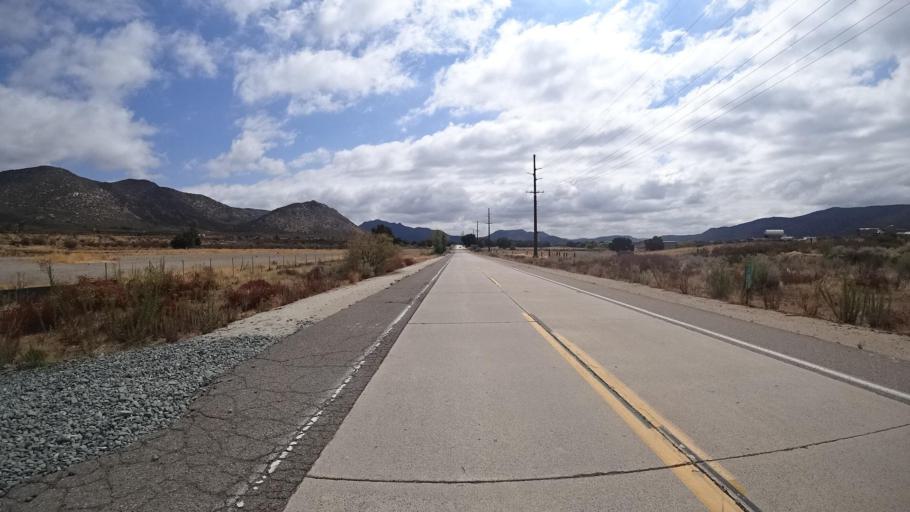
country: US
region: California
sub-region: San Diego County
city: Pine Valley
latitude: 32.7627
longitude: -116.4887
